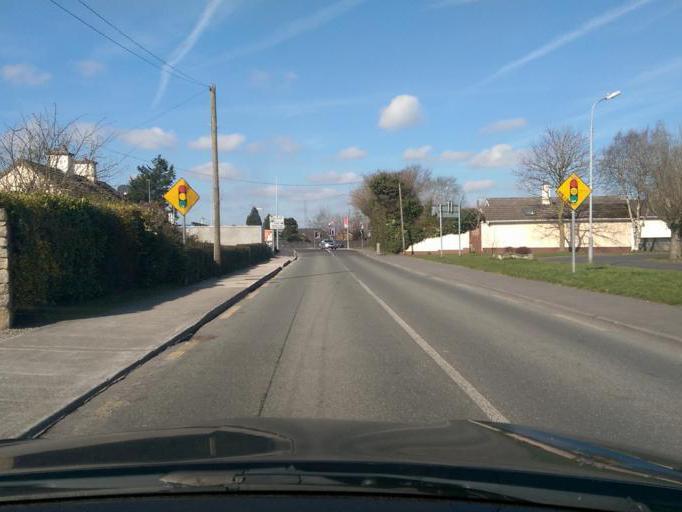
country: IE
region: Leinster
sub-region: Kildare
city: Maynooth
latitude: 53.3743
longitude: -6.5869
